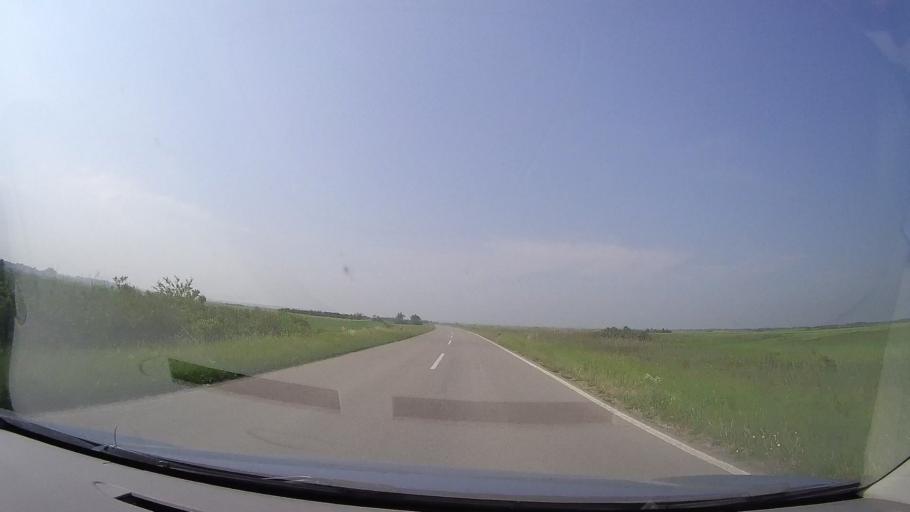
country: RS
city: Jasa Tomic
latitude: 45.4272
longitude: 20.8378
